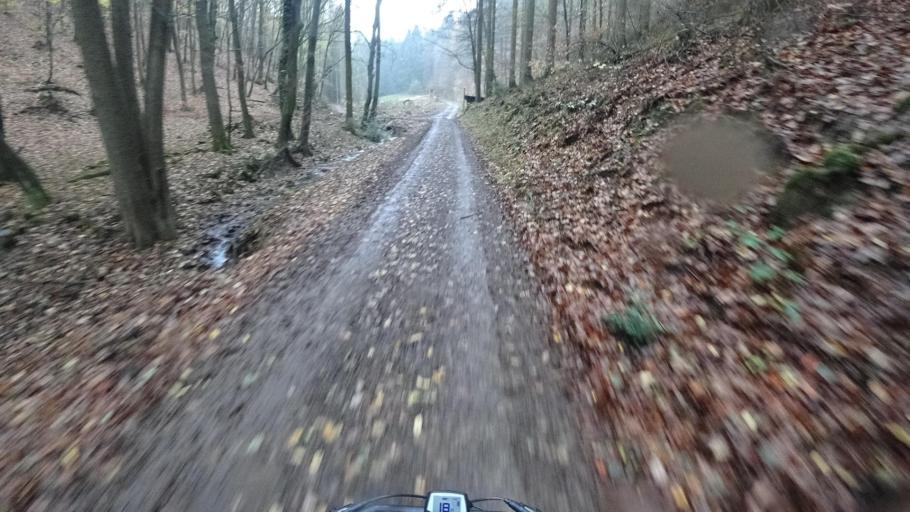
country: DE
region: Rheinland-Pfalz
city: Bad Neuenahr-Ahrweiler
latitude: 50.5151
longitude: 7.0932
